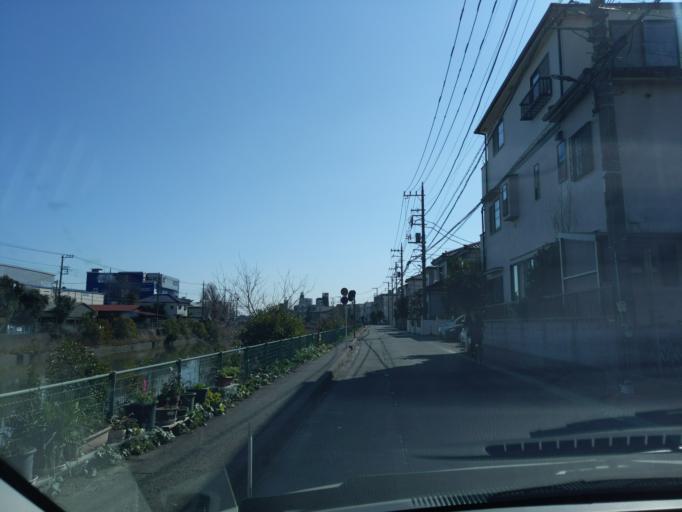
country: JP
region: Saitama
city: Soka
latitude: 35.8335
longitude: 139.8100
